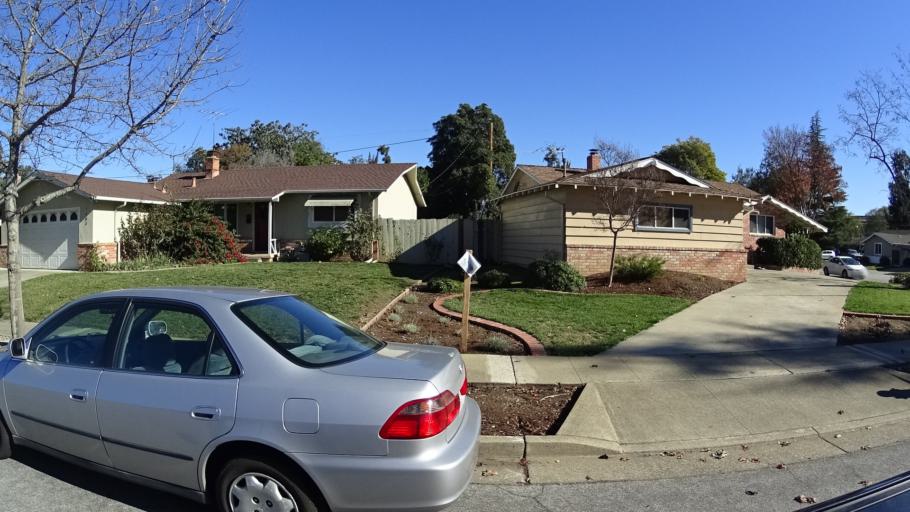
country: US
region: California
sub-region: Santa Clara County
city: Cupertino
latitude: 37.3387
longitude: -122.0133
